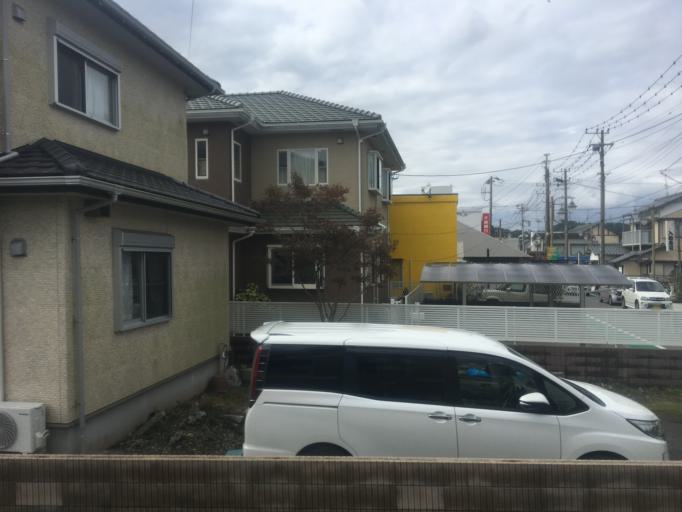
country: JP
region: Chiba
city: Ohara
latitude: 35.2493
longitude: 140.3909
